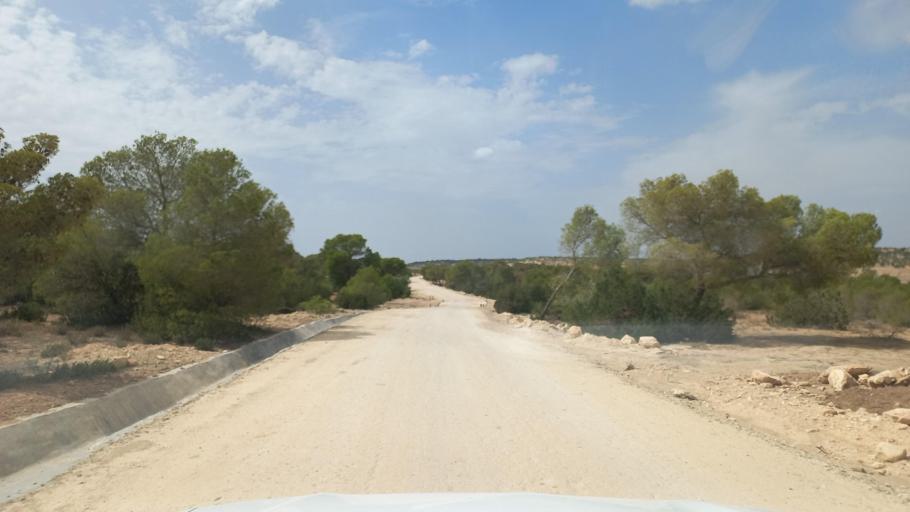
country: TN
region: Al Qasrayn
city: Kasserine
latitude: 35.3833
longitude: 8.8731
